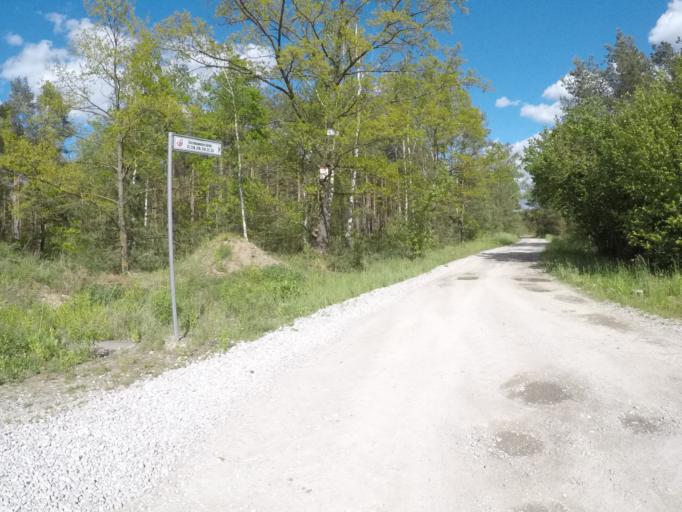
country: PL
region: Swietokrzyskie
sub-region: Powiat kielecki
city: Kostomloty Drugie
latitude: 50.8847
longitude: 20.5279
